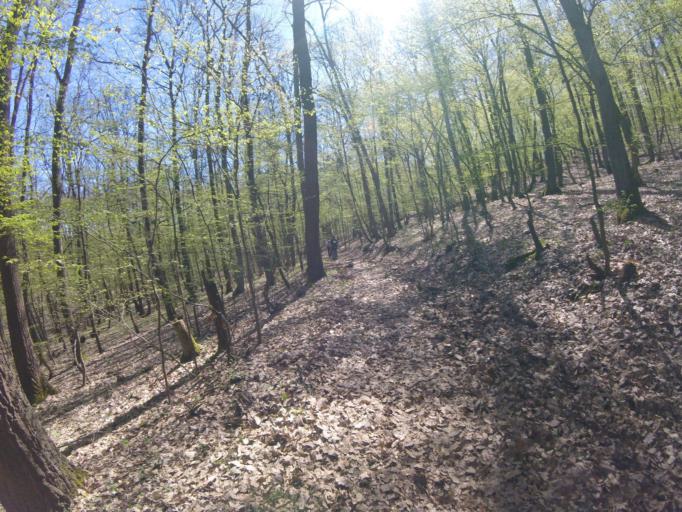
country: HU
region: Borsod-Abauj-Zemplen
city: Szendro
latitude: 48.4080
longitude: 20.7682
